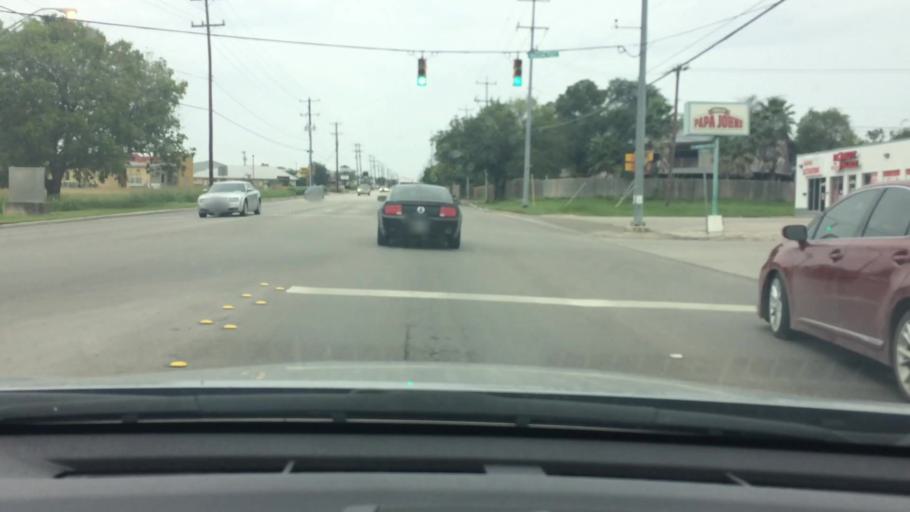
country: US
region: Texas
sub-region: Bexar County
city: Live Oak
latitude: 29.5399
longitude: -98.3379
